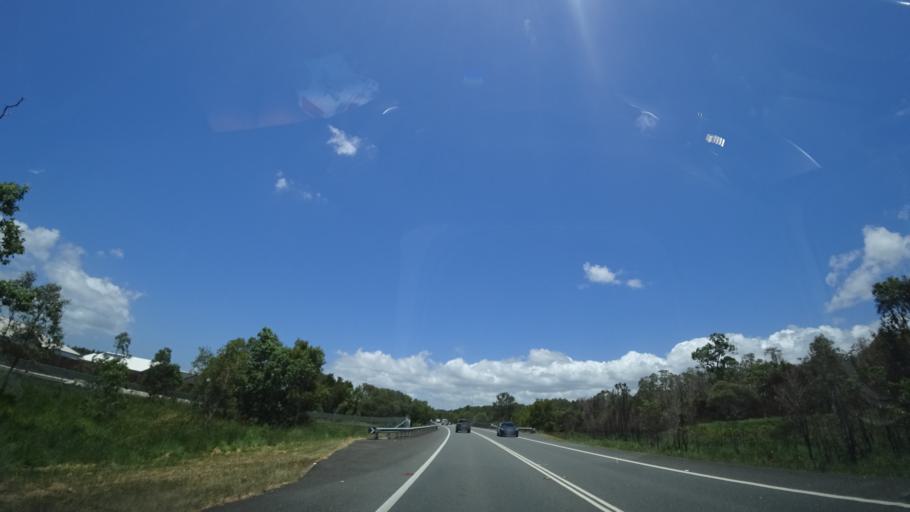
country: AU
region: Queensland
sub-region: Sunshine Coast
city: Little Mountain
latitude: -26.7733
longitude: 153.0799
